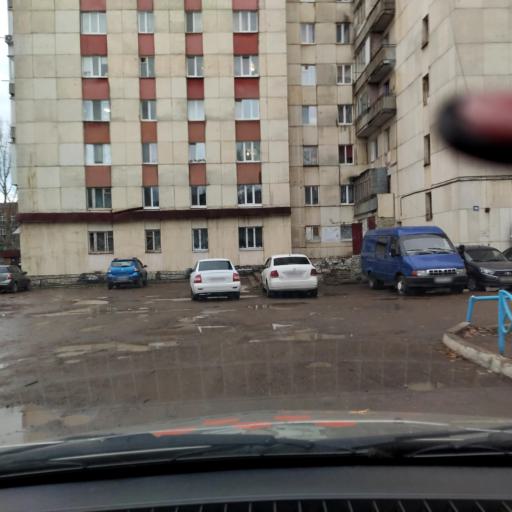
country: RU
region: Bashkortostan
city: Ufa
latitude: 54.7505
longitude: 56.0048
